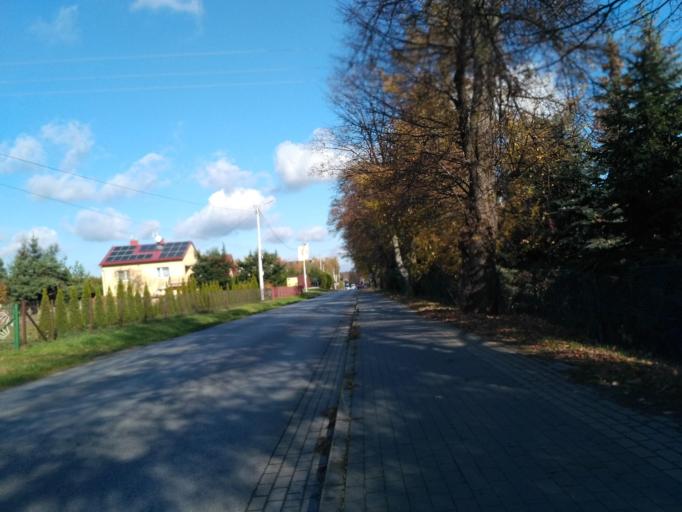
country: PL
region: Subcarpathian Voivodeship
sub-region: Powiat rzeszowski
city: Trzciana
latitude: 50.1125
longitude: 21.8588
